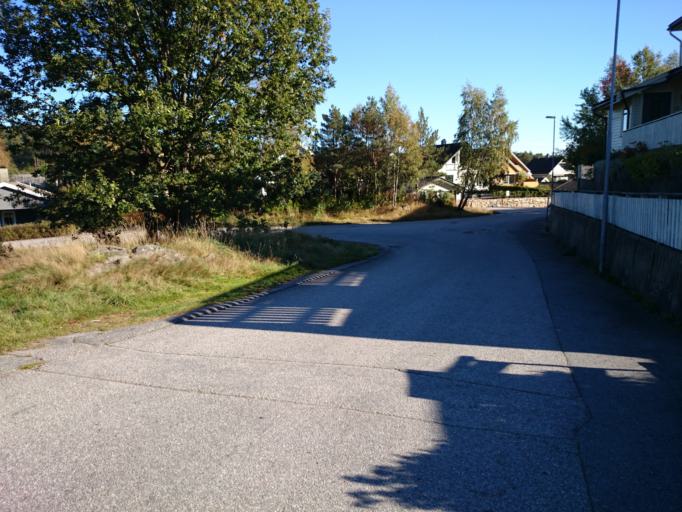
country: NO
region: Vest-Agder
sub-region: Kristiansand
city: Tveit
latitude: 58.1770
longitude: 8.0963
